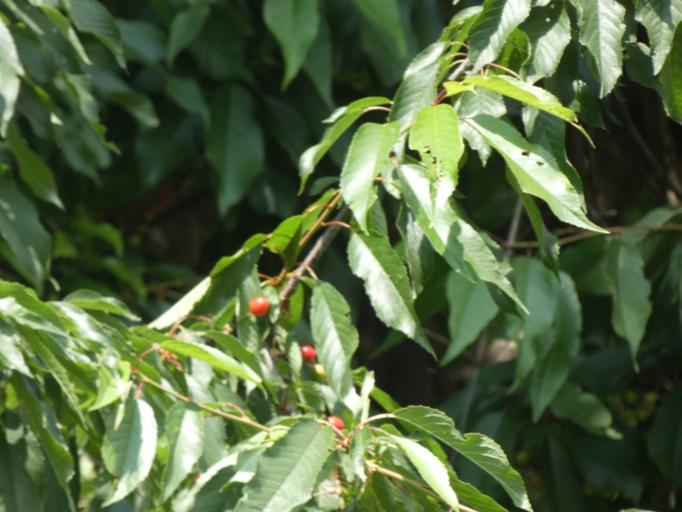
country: HU
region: Fejer
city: Szarliget
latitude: 47.5043
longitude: 18.4446
